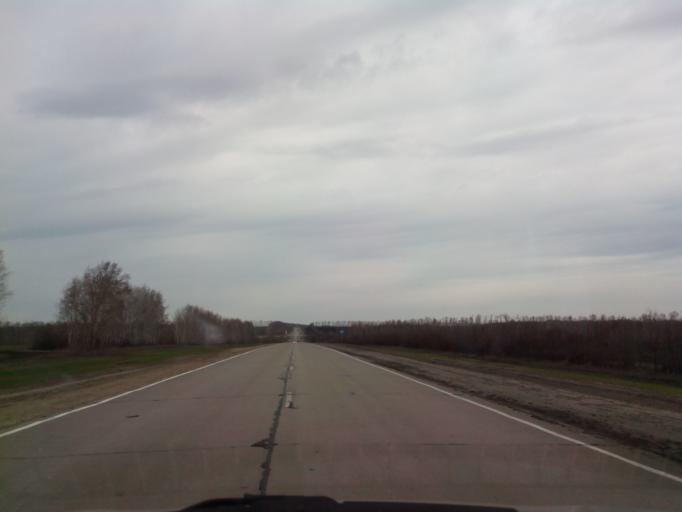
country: RU
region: Tambov
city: Znamenka
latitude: 52.4611
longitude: 41.3671
